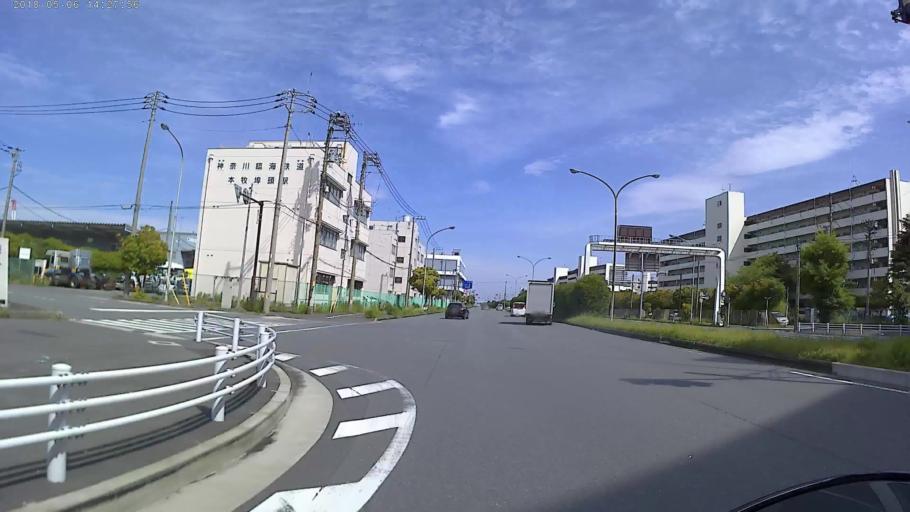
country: JP
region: Kanagawa
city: Yokohama
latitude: 35.4311
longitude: 139.6713
